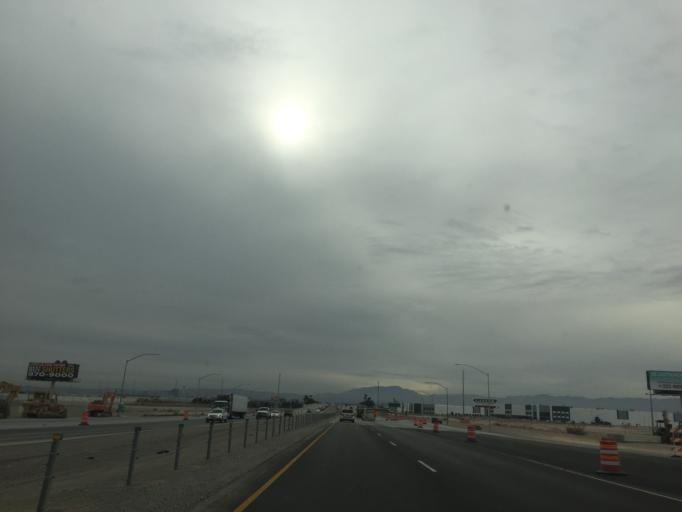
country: US
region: Nevada
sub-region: Clark County
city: Nellis Air Force Base
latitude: 36.2630
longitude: -115.0743
